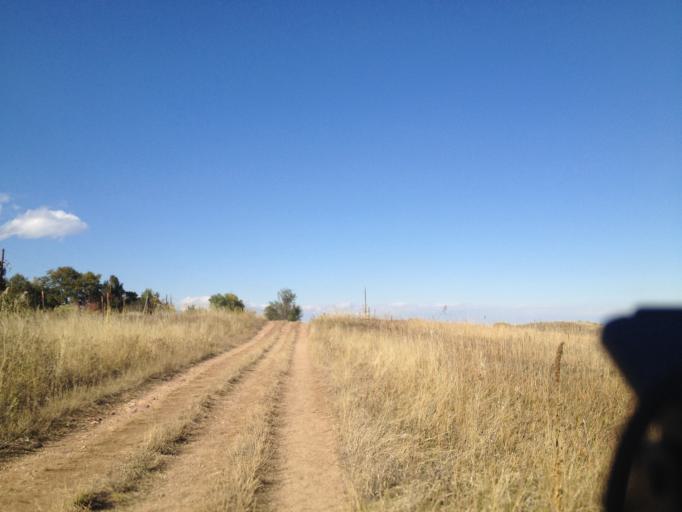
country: US
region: Colorado
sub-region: Boulder County
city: Boulder
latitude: 39.9732
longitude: -105.2365
